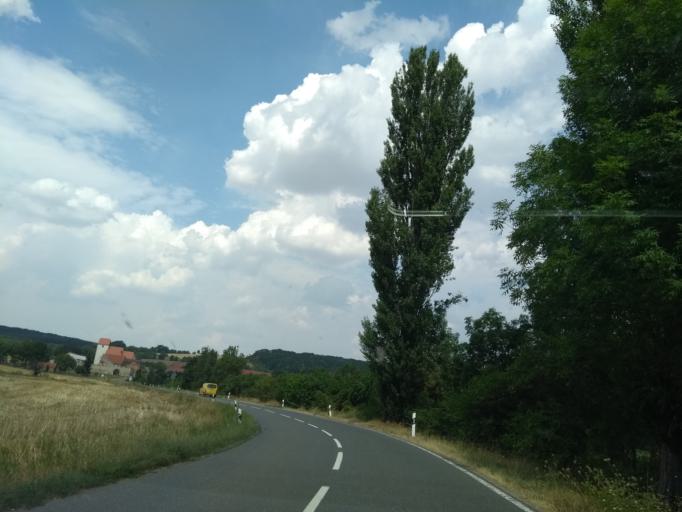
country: DE
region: Saxony-Anhalt
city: Wetterzeube
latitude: 51.0007
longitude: 11.9888
